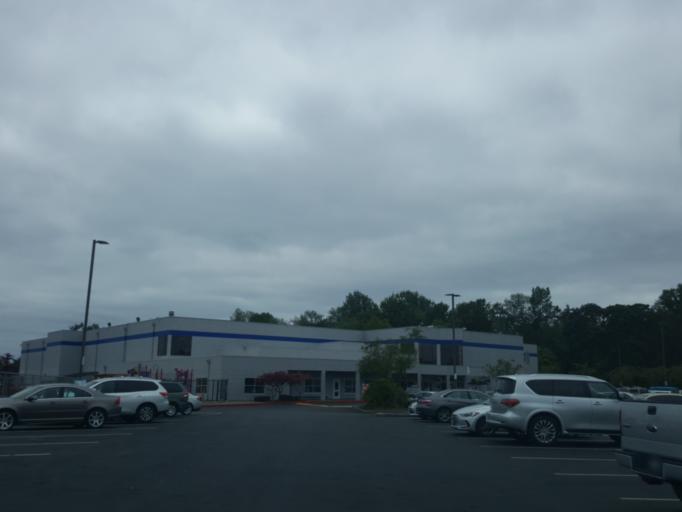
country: US
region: Washington
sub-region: Pierce County
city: Lakewood
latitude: 47.1690
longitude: -122.5035
